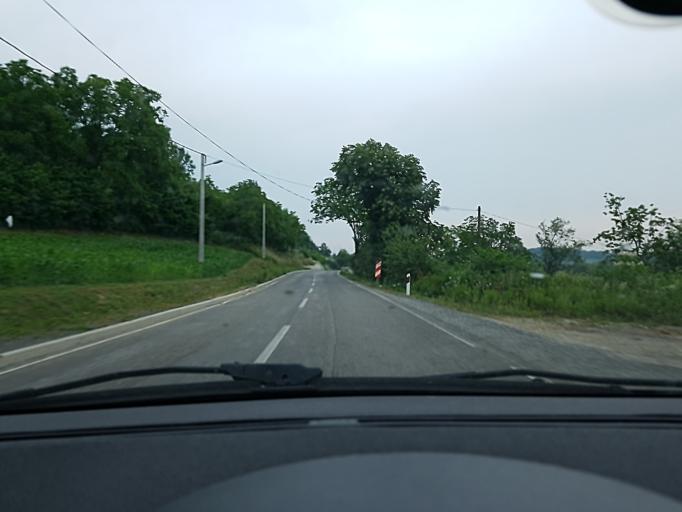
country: HR
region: Zagrebacka
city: Jakovlje
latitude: 46.0134
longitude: 15.8536
